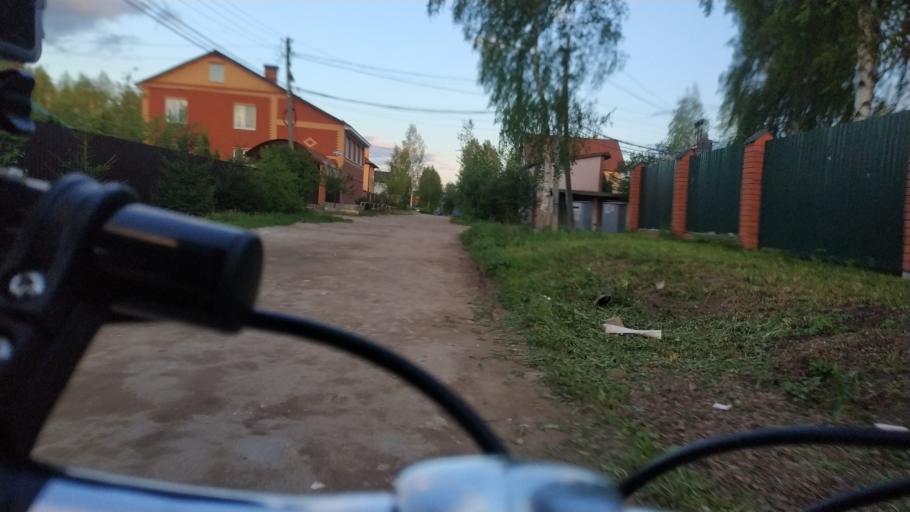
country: RU
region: Moskovskaya
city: Ramenskoye
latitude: 55.5705
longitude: 38.2776
